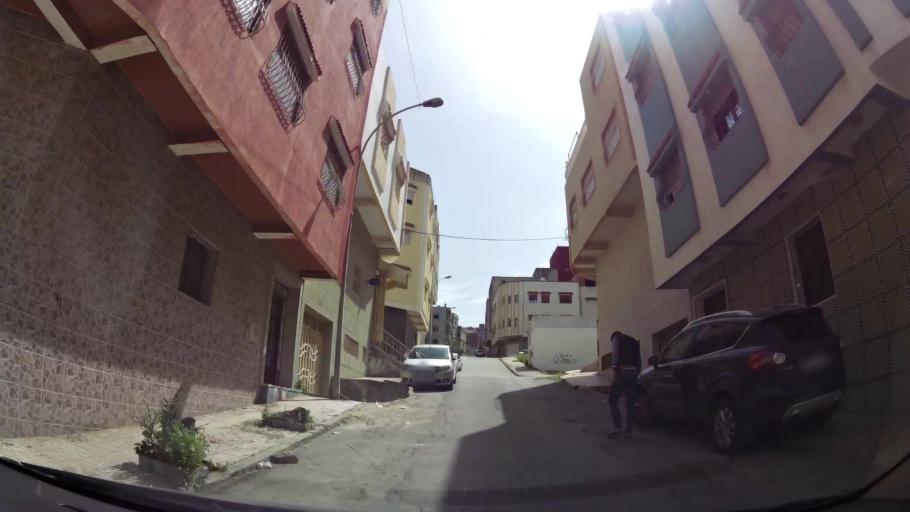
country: MA
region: Tanger-Tetouan
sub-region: Tanger-Assilah
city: Tangier
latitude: 35.7490
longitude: -5.8303
